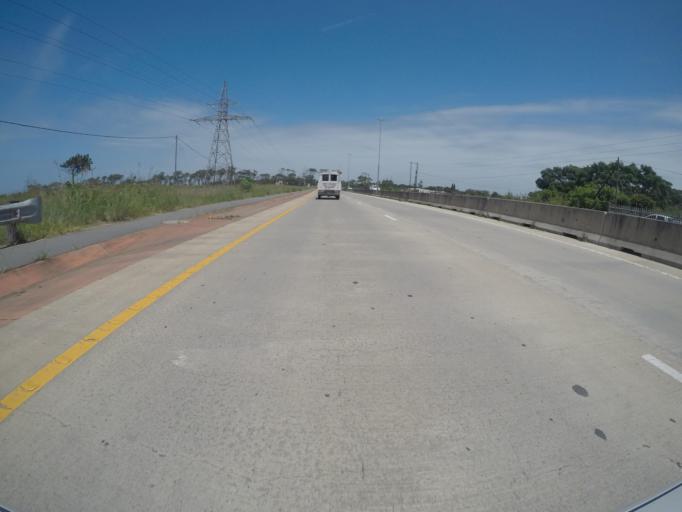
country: ZA
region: Eastern Cape
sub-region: Buffalo City Metropolitan Municipality
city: East London
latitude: -32.9361
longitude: 27.9870
